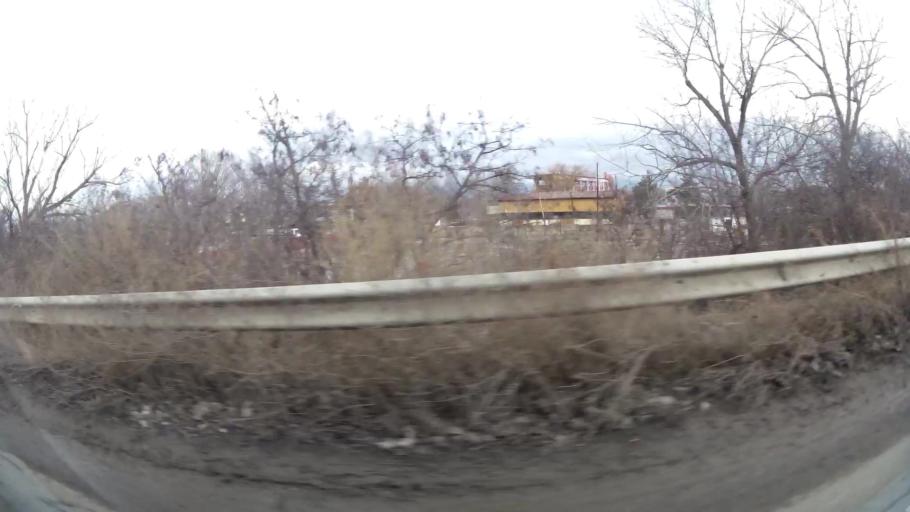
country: BG
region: Sofia-Capital
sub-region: Stolichna Obshtina
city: Sofia
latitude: 42.7500
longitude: 23.2769
